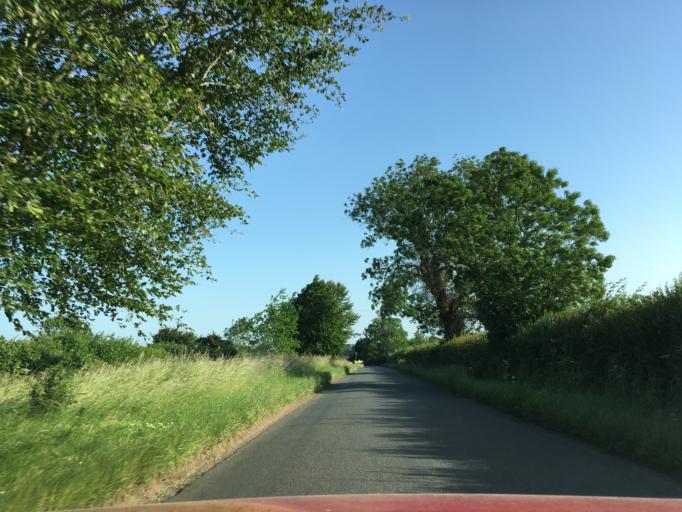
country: GB
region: England
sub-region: Gloucestershire
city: Fairford
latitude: 51.7143
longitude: -1.7679
